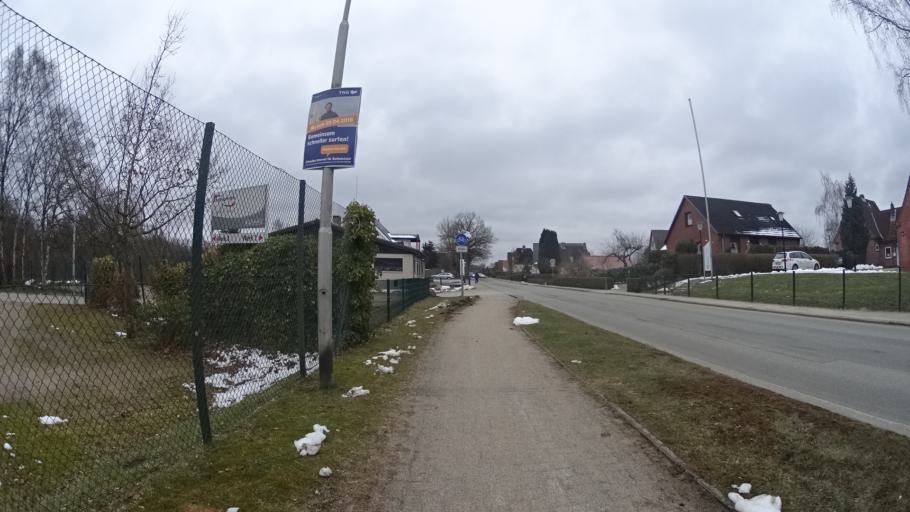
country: DE
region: Schleswig-Holstein
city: Malente
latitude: 54.1866
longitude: 10.5637
